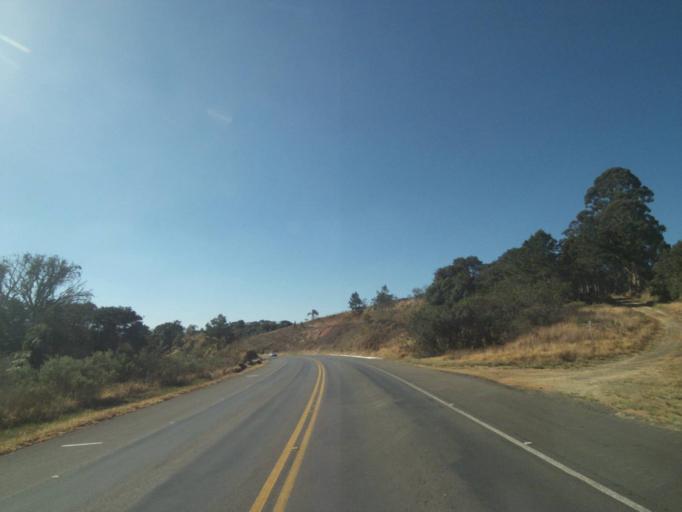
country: BR
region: Parana
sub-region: Tibagi
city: Tibagi
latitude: -24.7796
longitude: -50.4623
